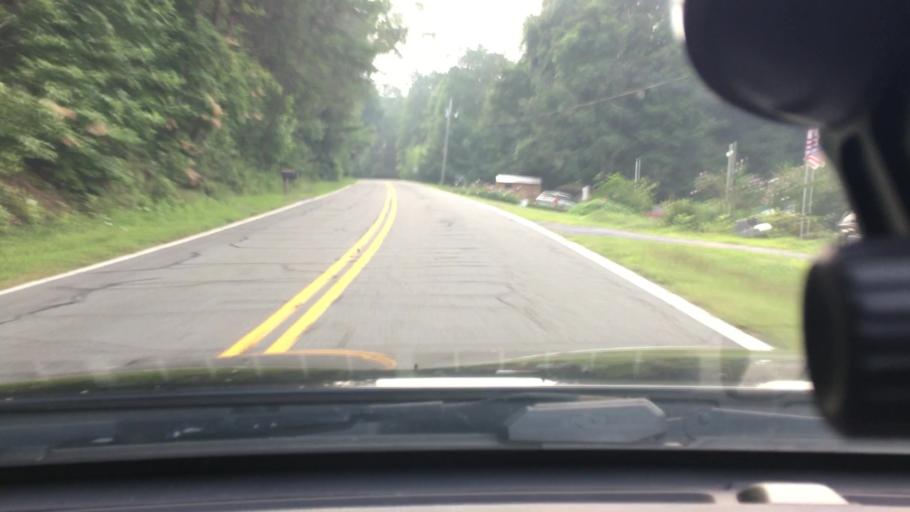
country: US
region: North Carolina
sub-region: Rutherford County
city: Rutherfordton
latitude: 35.3767
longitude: -81.9780
